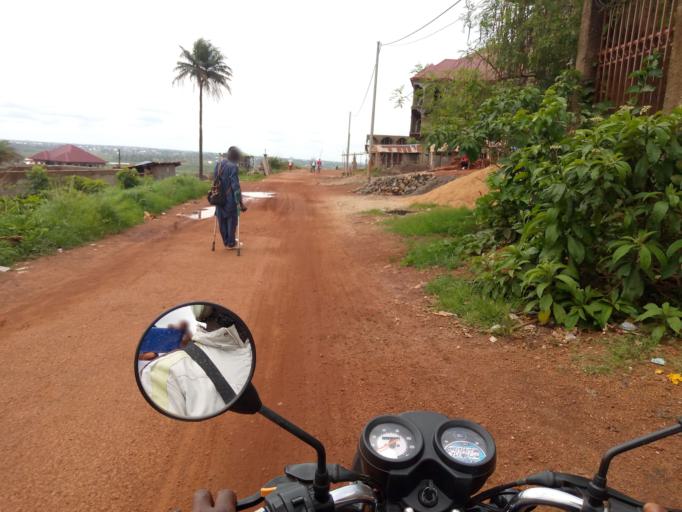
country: SL
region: Western Area
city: Waterloo
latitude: 8.3563
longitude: -13.0817
